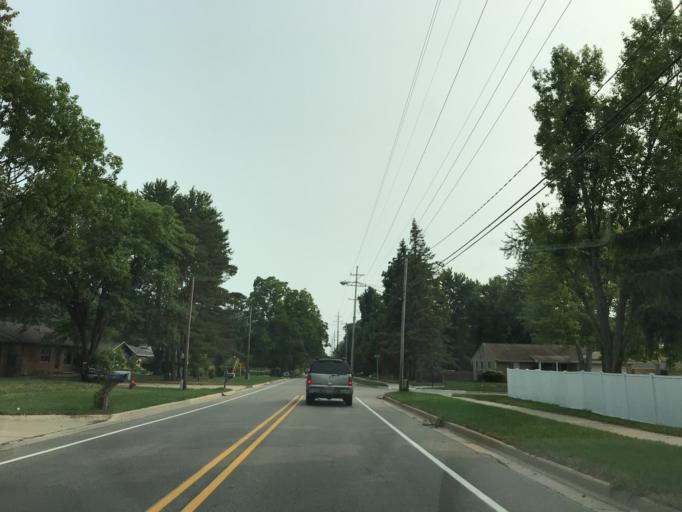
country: US
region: Michigan
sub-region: Ingham County
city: Okemos
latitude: 42.7382
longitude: -84.4474
